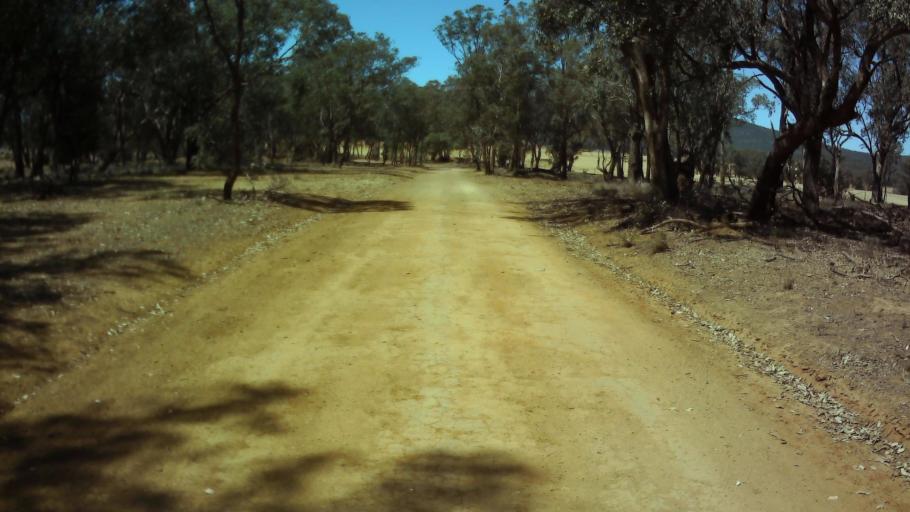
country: AU
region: New South Wales
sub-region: Weddin
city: Grenfell
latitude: -33.9547
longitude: 148.0844
